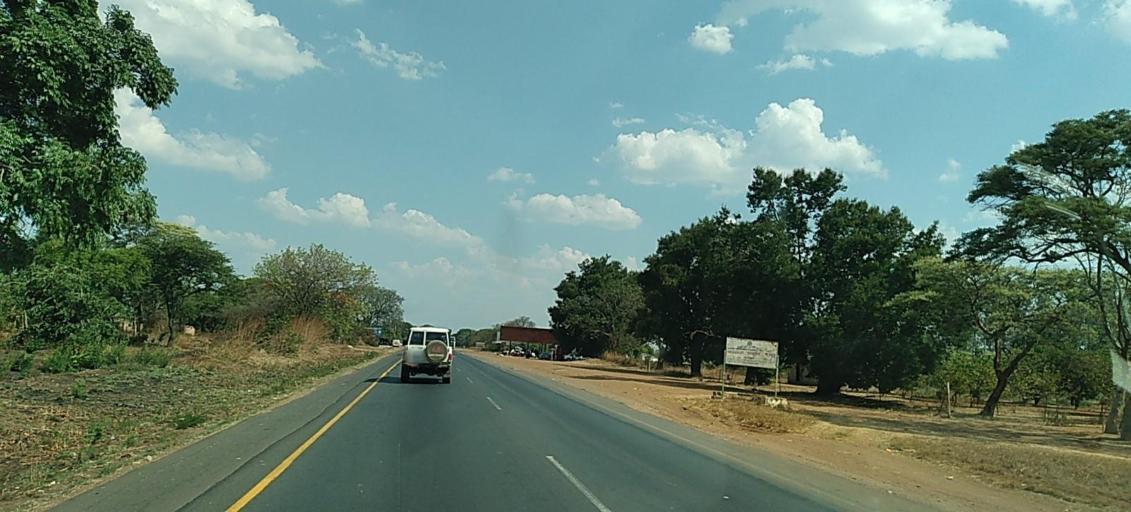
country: ZM
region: Central
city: Chibombo
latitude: -14.8787
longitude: 28.0603
